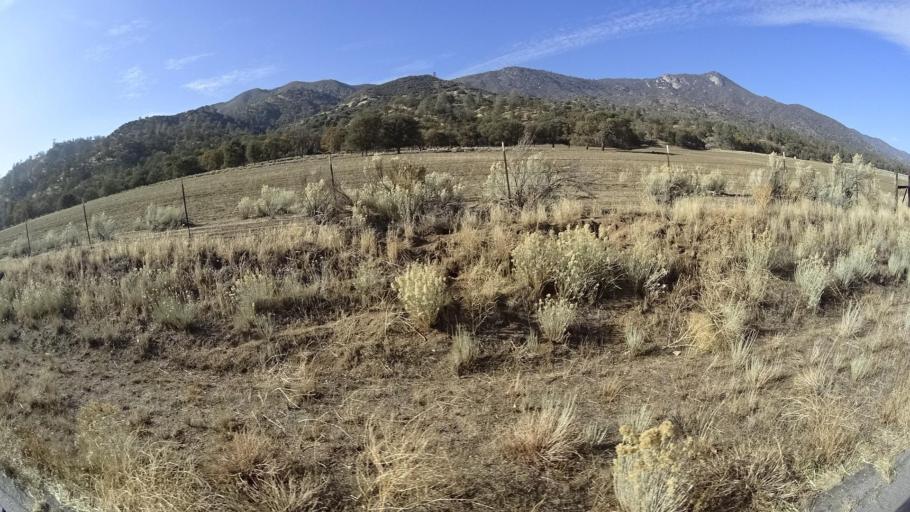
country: US
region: California
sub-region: Kern County
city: Bodfish
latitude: 35.4005
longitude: -118.5457
